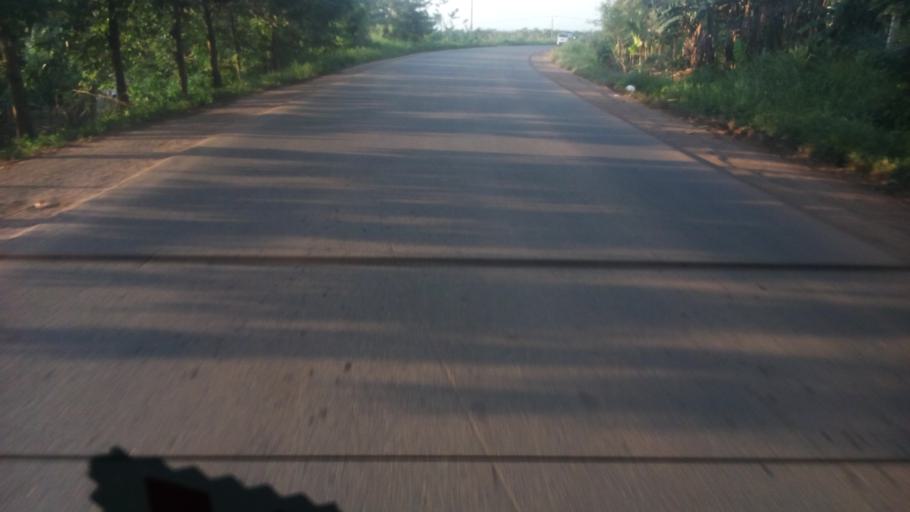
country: GH
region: Western
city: Tarkwa
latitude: 5.1594
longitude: -2.0749
